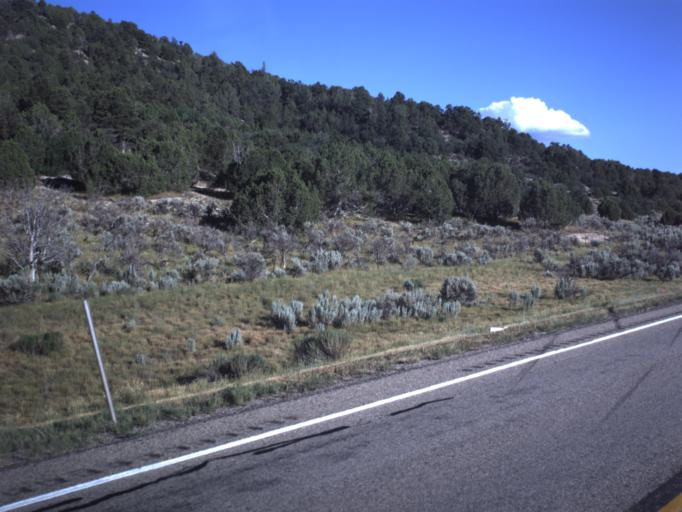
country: US
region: Utah
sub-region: Sanpete County
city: Fairview
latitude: 39.7403
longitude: -111.4773
